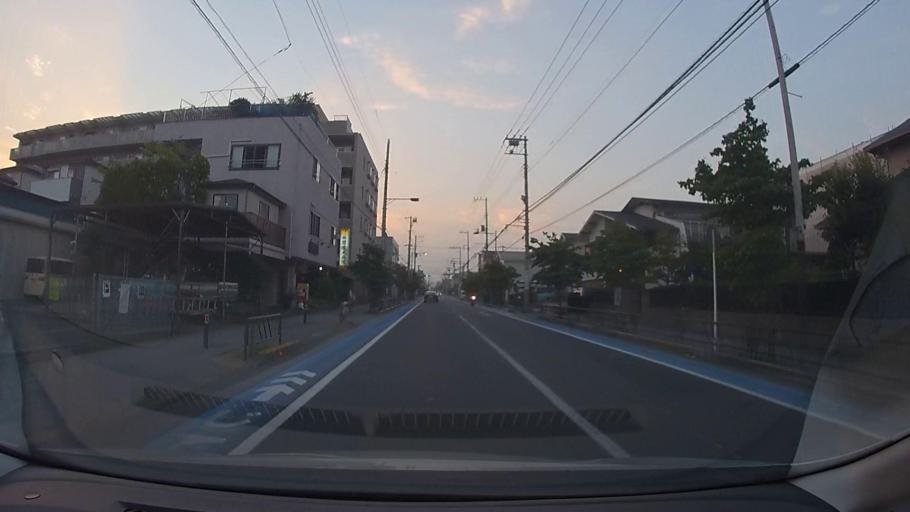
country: JP
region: Kanagawa
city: Minami-rinkan
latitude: 35.4906
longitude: 139.4473
